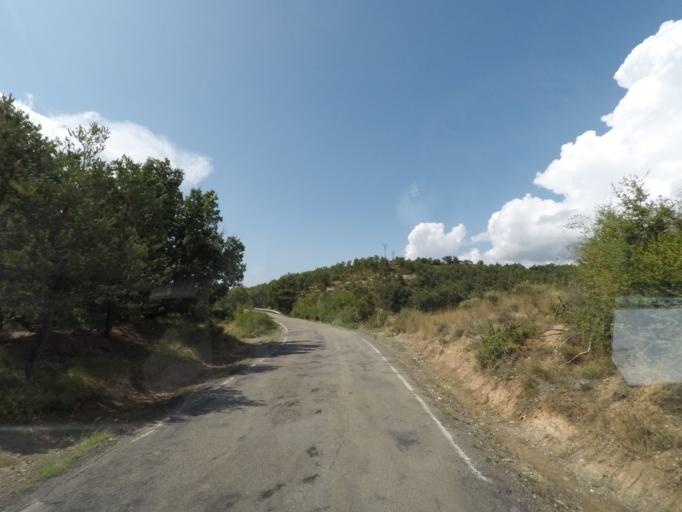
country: ES
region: Aragon
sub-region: Provincia de Huesca
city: Yebra de Basa
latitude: 42.3981
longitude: -0.3374
